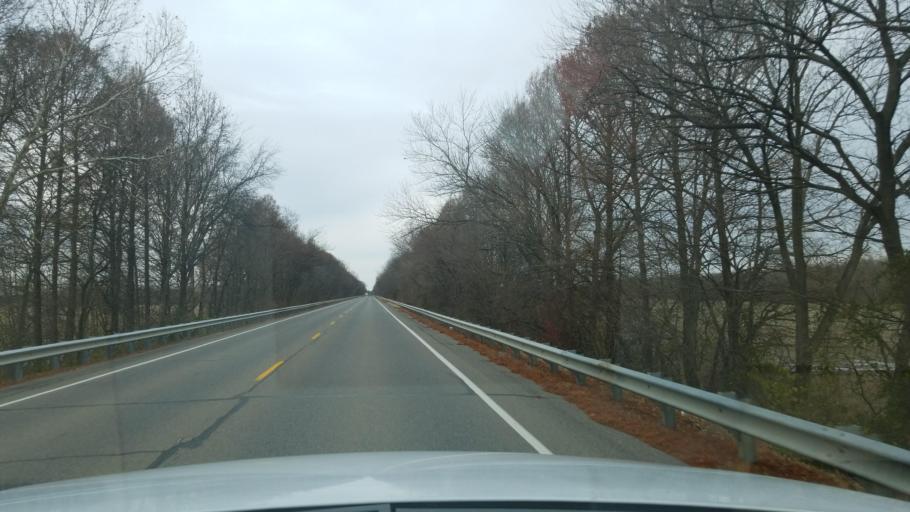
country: US
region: Indiana
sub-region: Posey County
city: Mount Vernon
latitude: 37.9290
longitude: -87.9671
